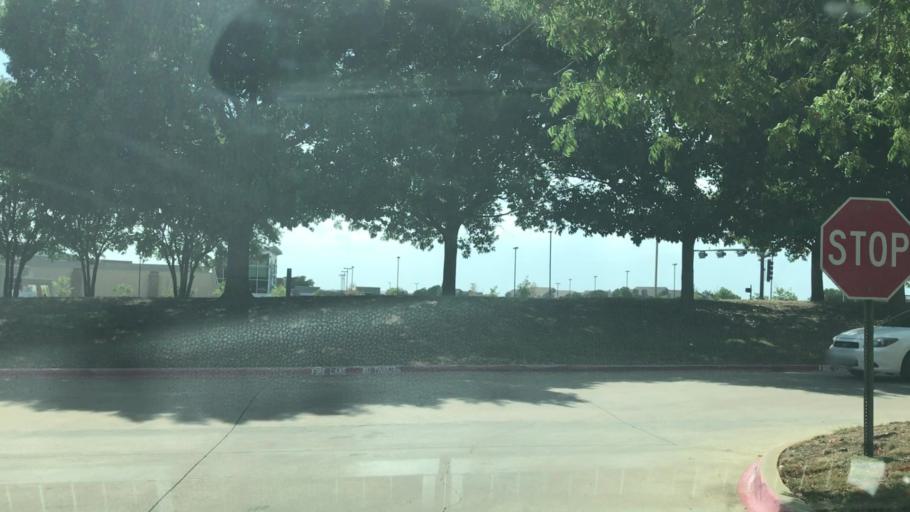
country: US
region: Texas
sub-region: Dallas County
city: Farmers Branch
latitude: 32.9016
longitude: -96.9582
